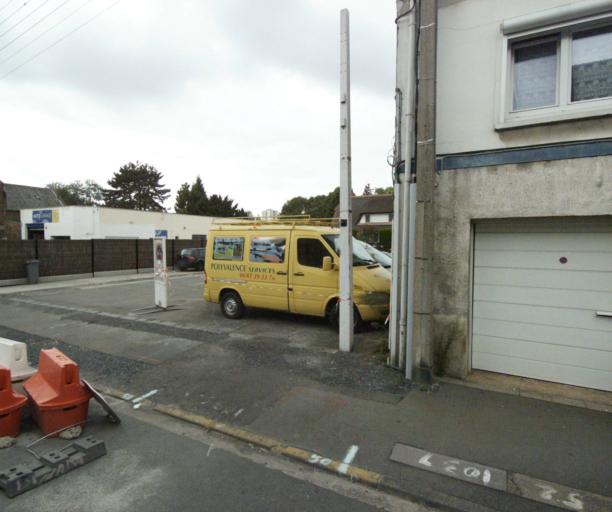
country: FR
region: Nord-Pas-de-Calais
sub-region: Departement du Nord
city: Mons-en-Baroeul
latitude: 50.6384
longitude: 3.1261
